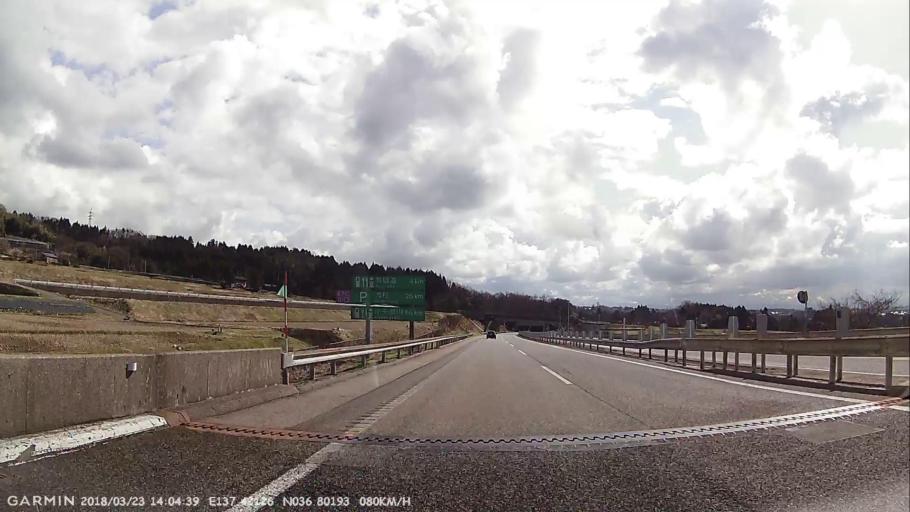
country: JP
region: Toyama
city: Uozu
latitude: 36.8017
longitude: 137.4212
